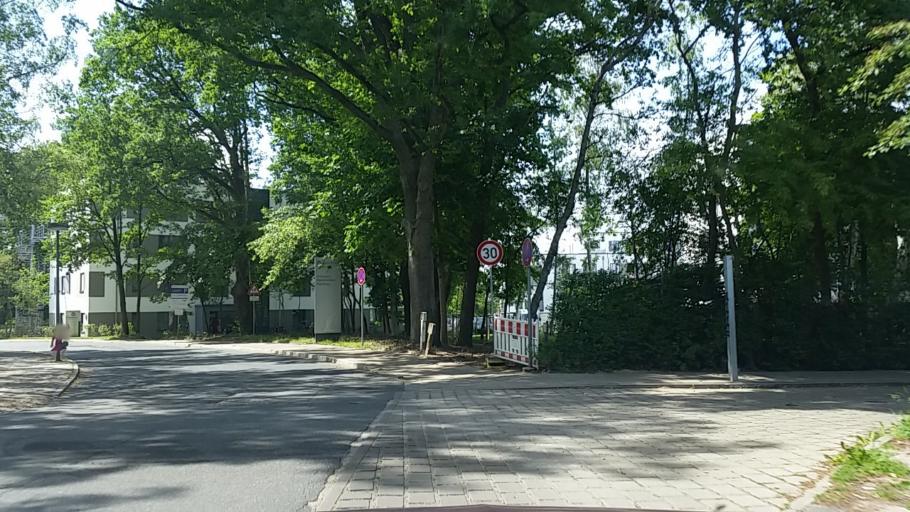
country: DE
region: Schleswig-Holstein
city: Rellingen
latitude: 53.5821
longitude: 9.7834
